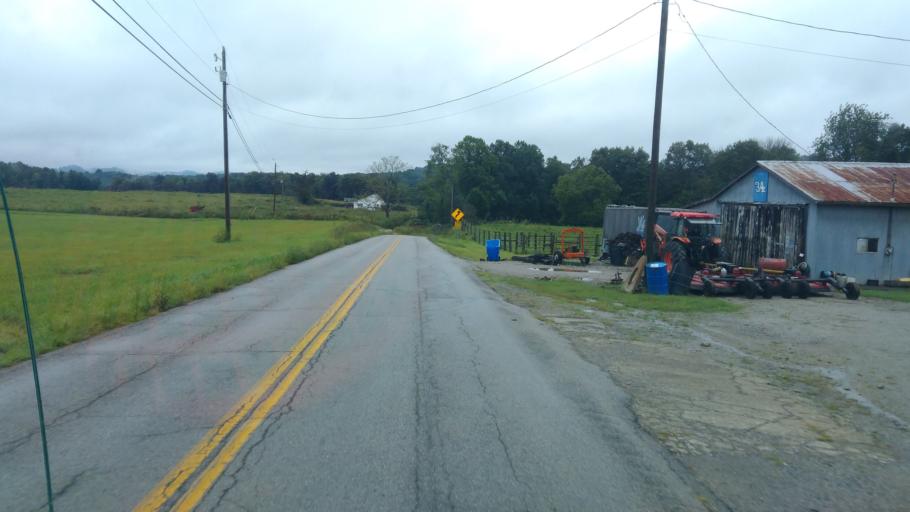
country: US
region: Kentucky
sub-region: Fleming County
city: Flemingsburg
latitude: 38.4555
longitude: -83.5213
